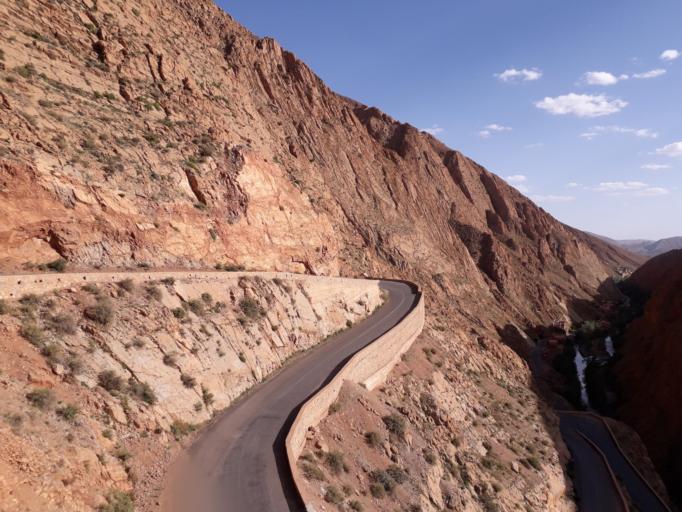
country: MA
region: Souss-Massa-Draa
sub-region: Ouarzazate
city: Imider
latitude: 31.5294
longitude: -5.9245
